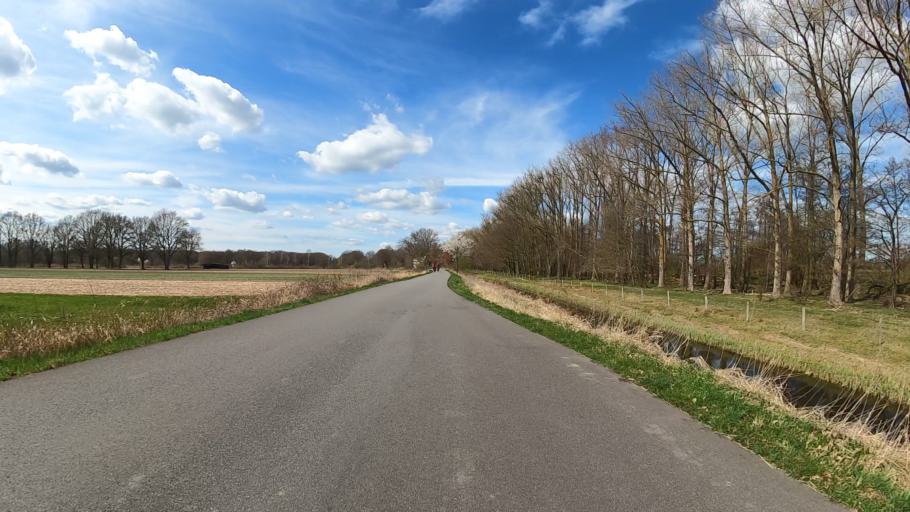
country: DE
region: Lower Saxony
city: Winsen
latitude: 53.4041
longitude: 10.2159
